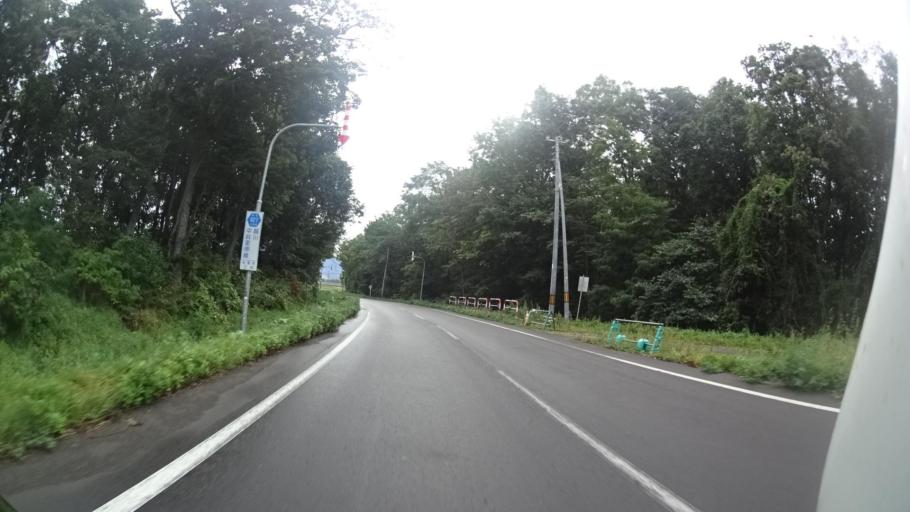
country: JP
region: Hokkaido
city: Abashiri
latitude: 43.8718
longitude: 144.6858
